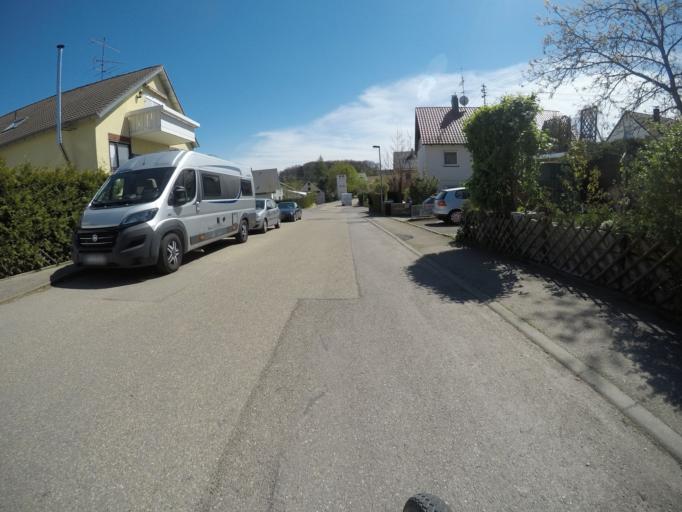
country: DE
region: Baden-Wuerttemberg
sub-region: Regierungsbezirk Stuttgart
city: Herrenberg
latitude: 48.5799
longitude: 8.8347
